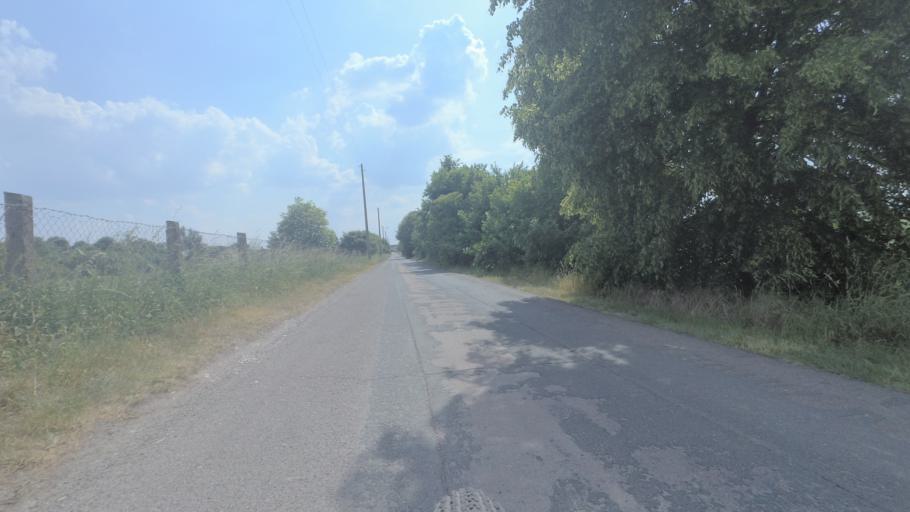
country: DE
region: Saxony-Anhalt
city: Koethen
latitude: 51.7651
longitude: 11.9322
